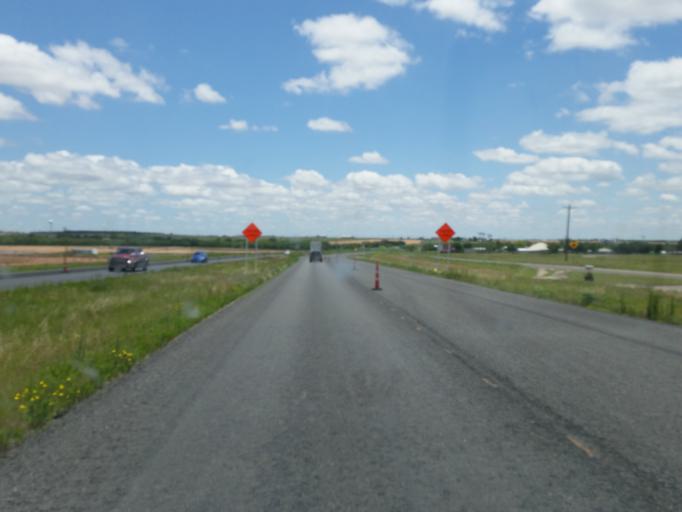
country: US
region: Texas
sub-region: Scurry County
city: Snyder
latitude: 32.7230
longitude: -100.8875
